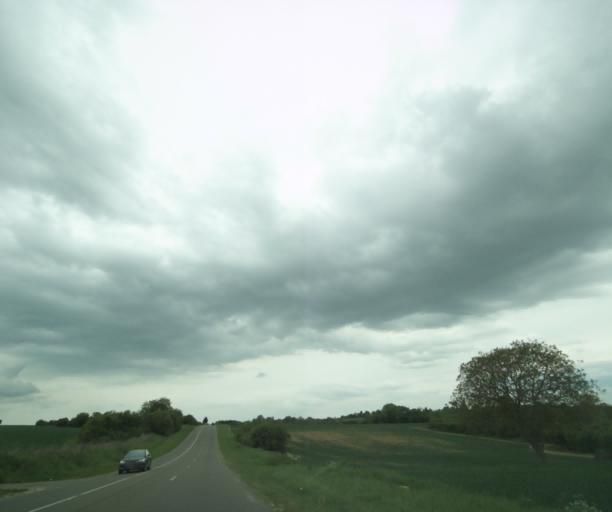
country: FR
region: Ile-de-France
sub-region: Departement des Yvelines
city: Bouafle
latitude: 48.9546
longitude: 1.9022
